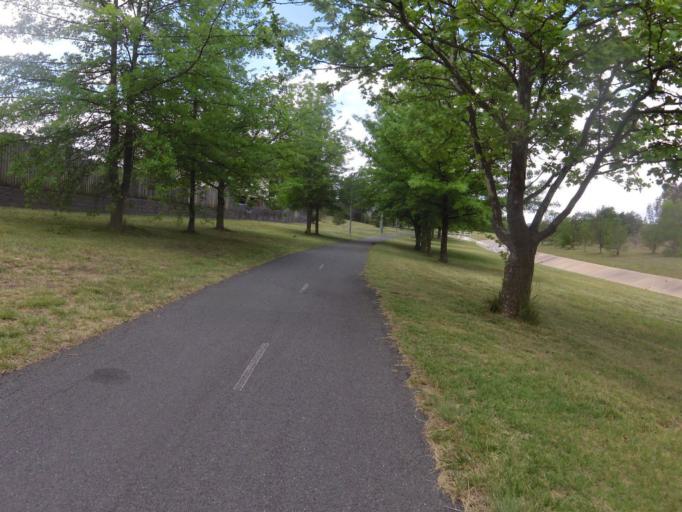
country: AU
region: Australian Capital Territory
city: Macarthur
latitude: -35.4191
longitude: 149.1063
